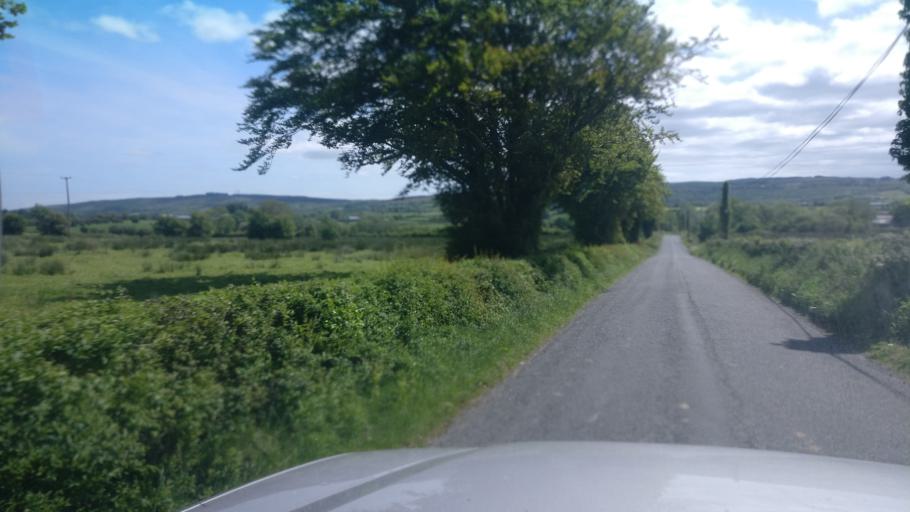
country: IE
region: Connaught
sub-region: County Galway
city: Gort
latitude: 53.1449
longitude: -8.7354
